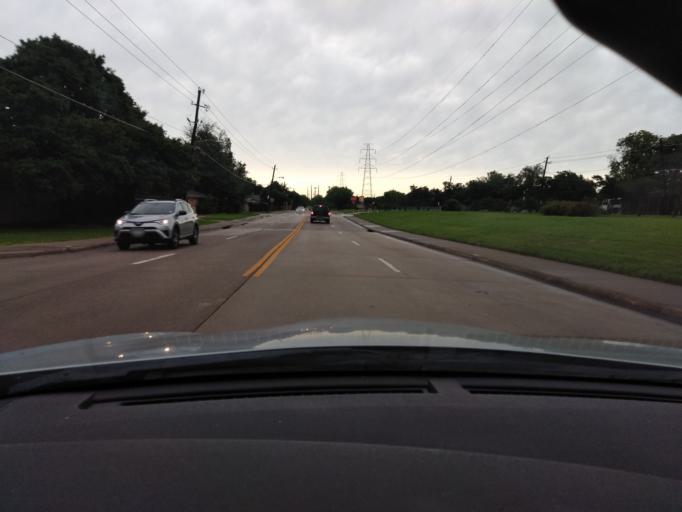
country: US
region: Texas
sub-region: Dallas County
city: Addison
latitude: 32.9695
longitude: -96.7785
